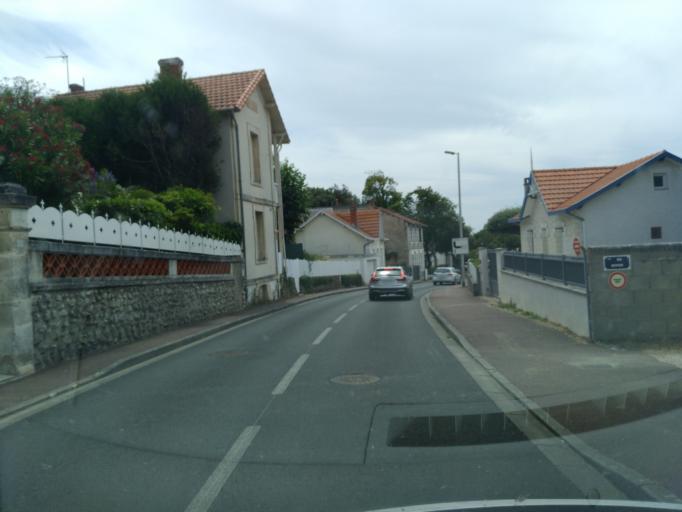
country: FR
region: Poitou-Charentes
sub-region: Departement de la Charente-Maritime
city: Saint-Palais-sur-Mer
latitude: 45.6438
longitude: -1.0853
